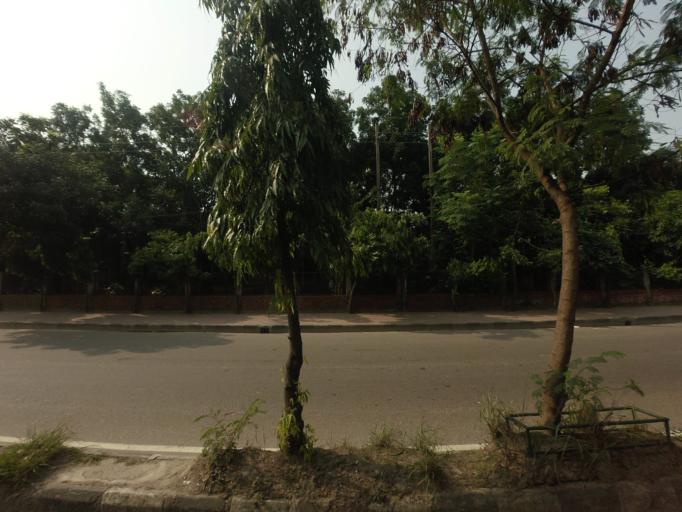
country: BD
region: Dhaka
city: Azimpur
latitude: 23.7754
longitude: 90.3752
